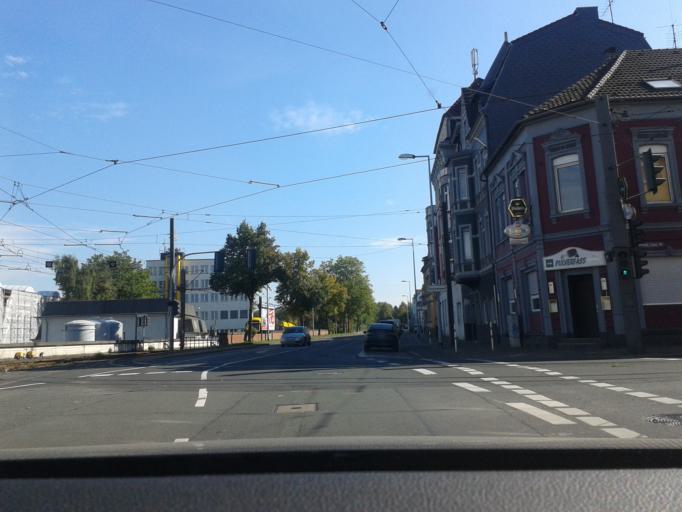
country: DE
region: North Rhine-Westphalia
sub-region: Regierungsbezirk Dusseldorf
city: Muelheim (Ruhr)
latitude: 51.4265
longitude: 6.8629
